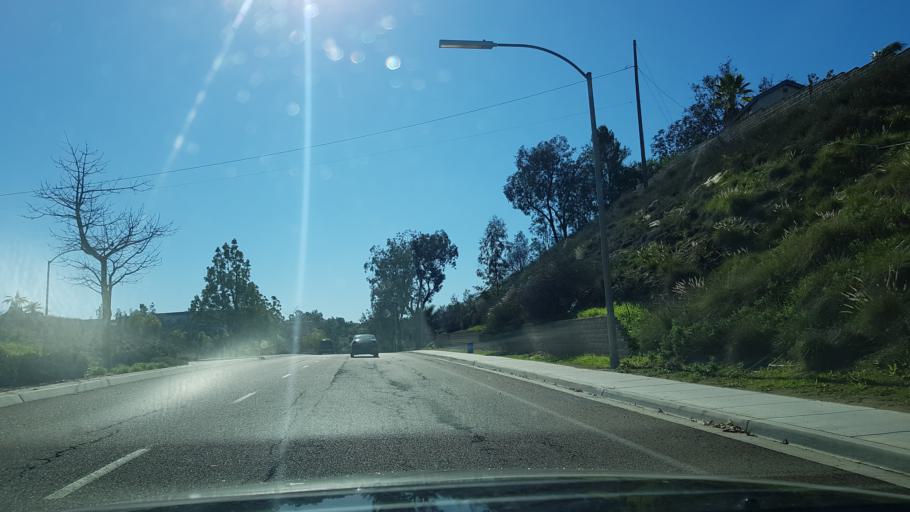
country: US
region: California
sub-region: San Diego County
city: Escondido
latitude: 33.1058
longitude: -117.1048
